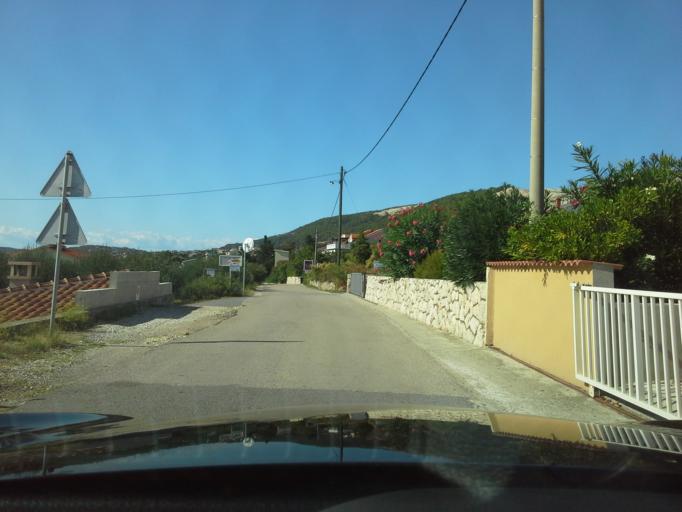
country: HR
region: Primorsko-Goranska
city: Banjol
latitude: 44.7365
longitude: 14.8003
